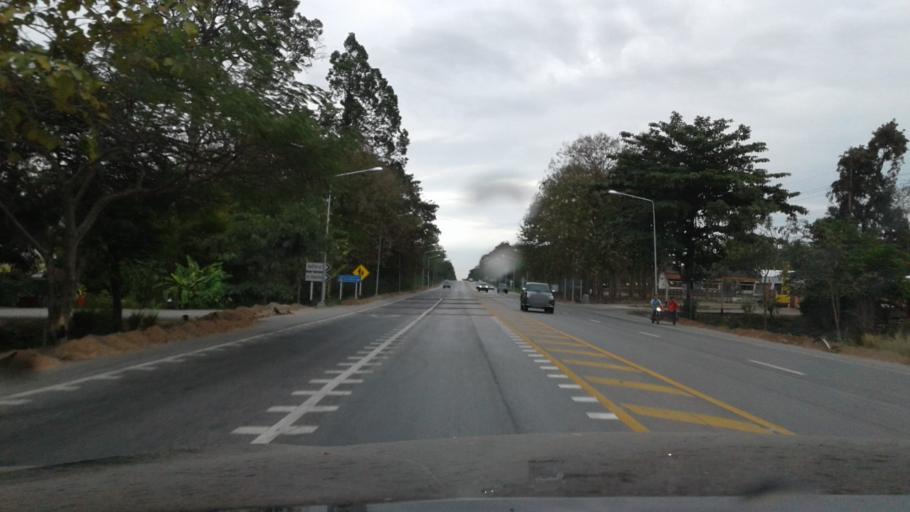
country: TH
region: Changwat Udon Thani
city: Nong Wua So
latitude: 17.2475
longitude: 102.5597
